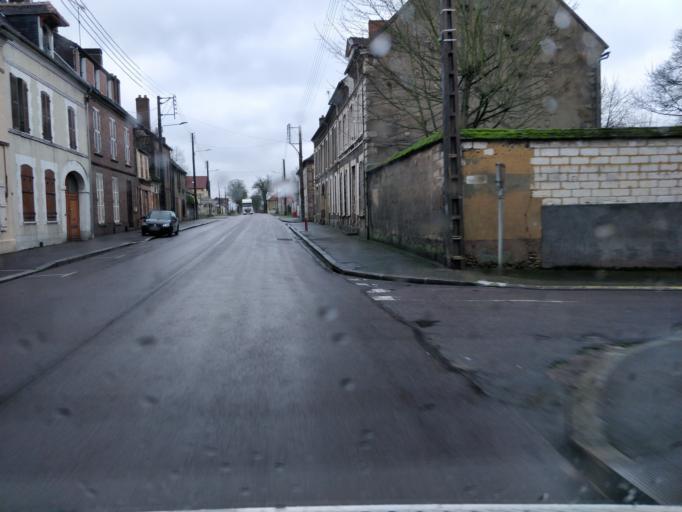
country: FR
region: Bourgogne
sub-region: Departement de l'Yonne
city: Thorigny-sur-Oreuse
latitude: 48.2367
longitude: 3.5599
